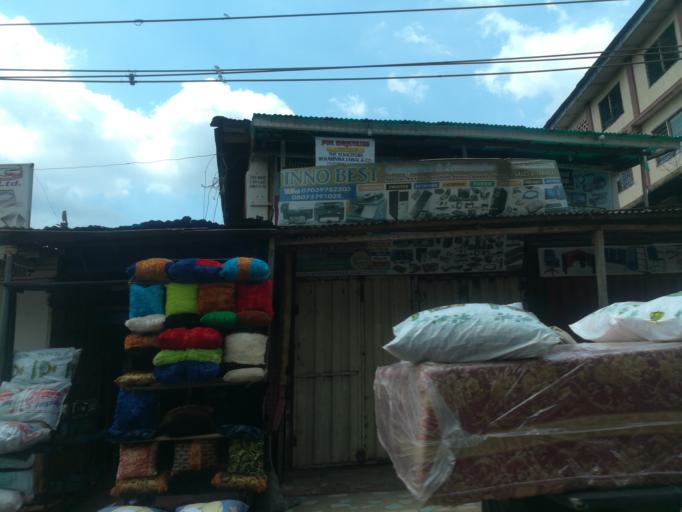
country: NG
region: Oyo
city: Ibadan
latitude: 7.3924
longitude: 3.8833
